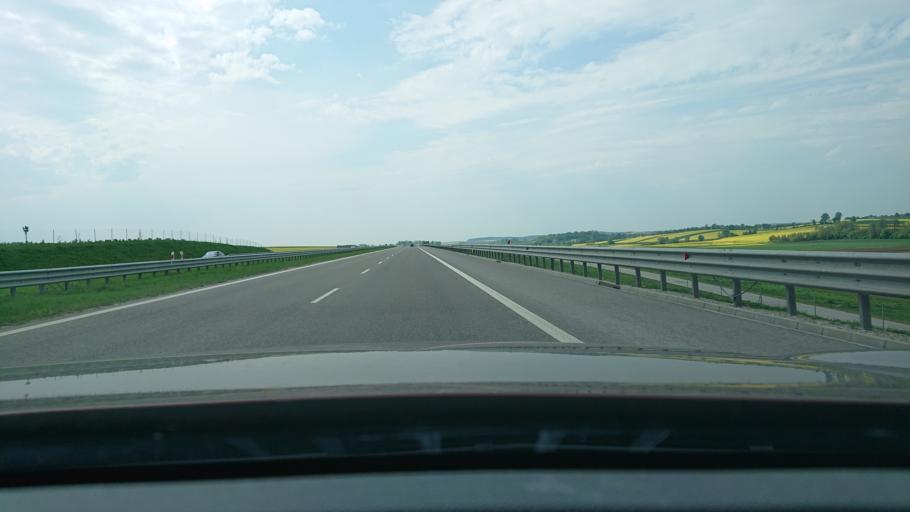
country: PL
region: Subcarpathian Voivodeship
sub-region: Powiat jaroslawski
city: Rokietnica
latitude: 49.9339
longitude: 22.6994
